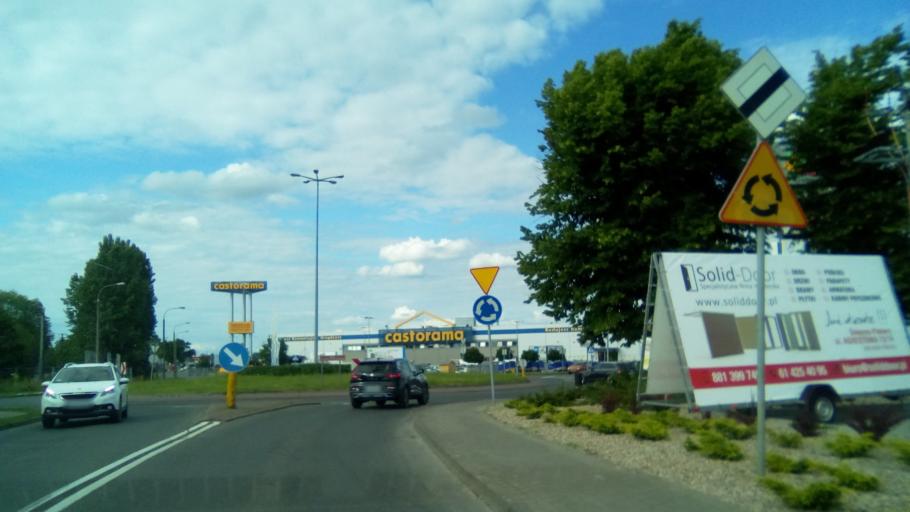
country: PL
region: Greater Poland Voivodeship
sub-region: Powiat gnieznienski
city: Gniezno
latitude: 52.5613
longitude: 17.6095
